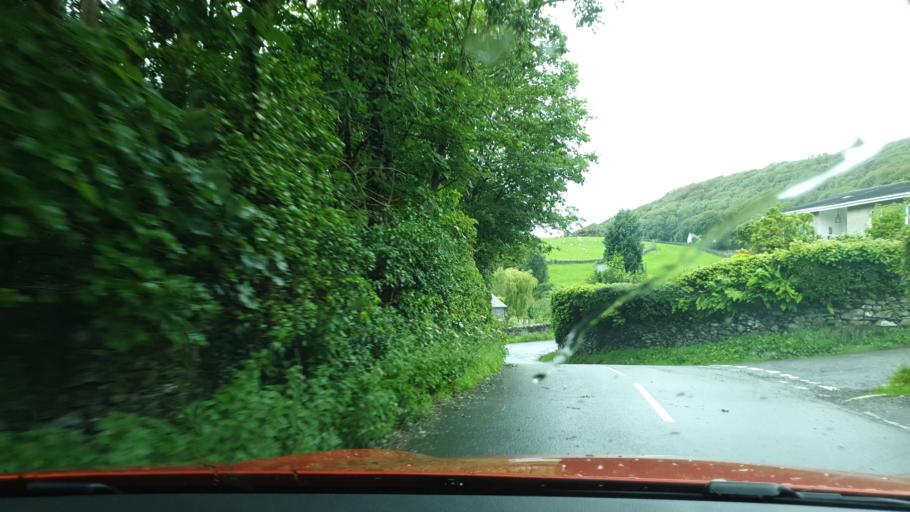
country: GB
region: England
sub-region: Cumbria
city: Ulverston
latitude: 54.2548
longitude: -3.0650
